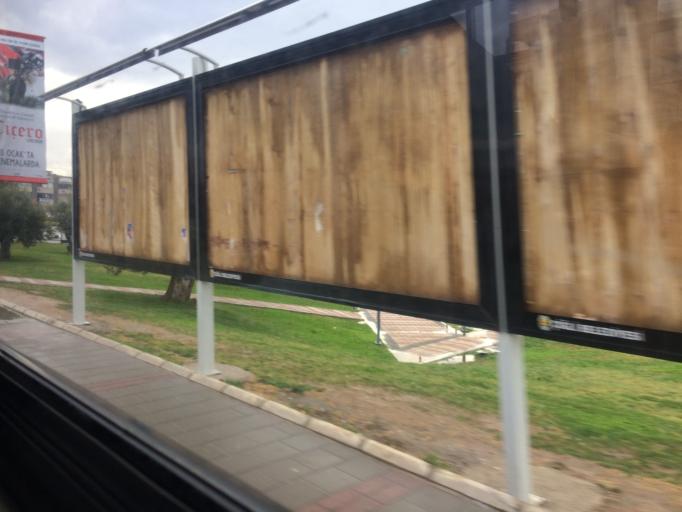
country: TR
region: Izmir
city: Karsiyaka
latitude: 38.4950
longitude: 27.0608
